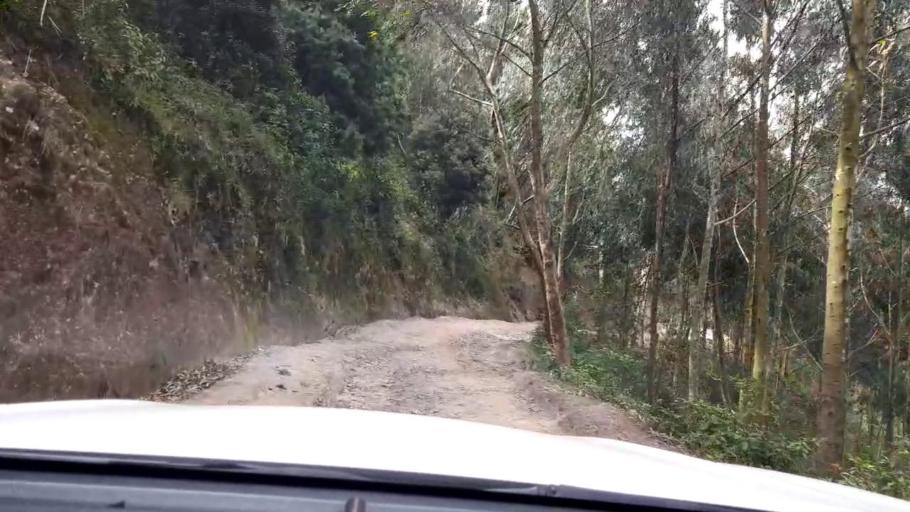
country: RW
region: Western Province
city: Kibuye
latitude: -1.8702
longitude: 29.4510
